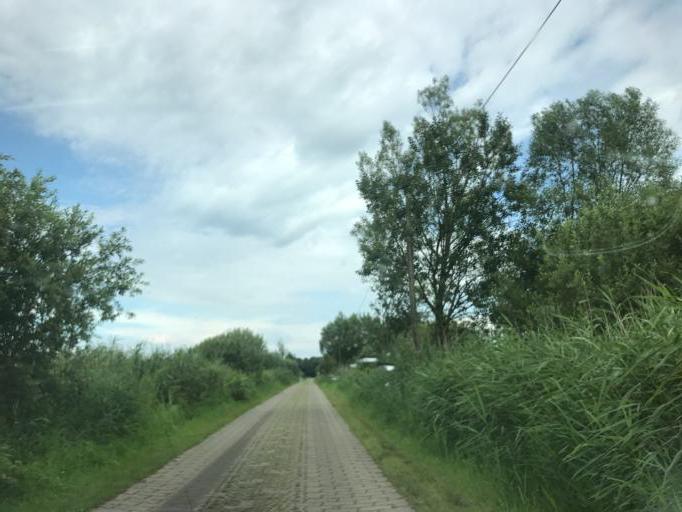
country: DE
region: Mecklenburg-Vorpommern
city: Wesenberg
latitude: 53.3901
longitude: 12.8940
